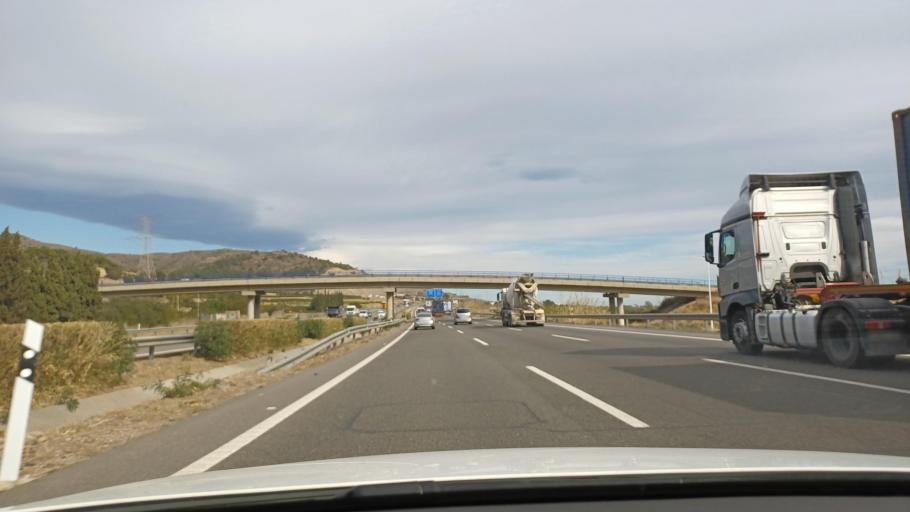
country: ES
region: Valencia
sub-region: Provincia de Valencia
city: Petres
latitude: 39.6903
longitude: -0.2859
